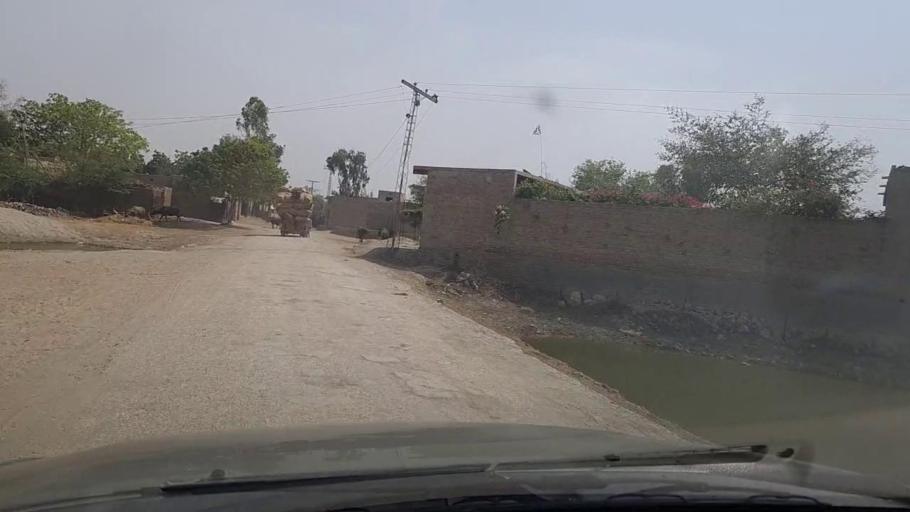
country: PK
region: Sindh
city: Lakhi
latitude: 27.9125
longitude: 68.6873
